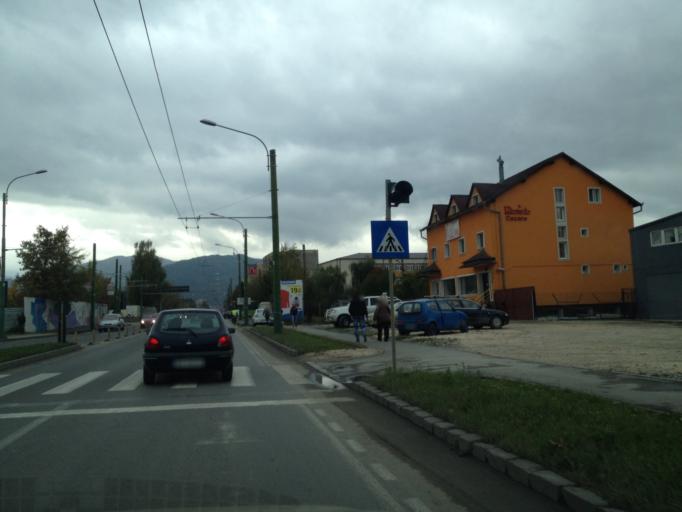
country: RO
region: Brasov
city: Brasov
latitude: 45.6713
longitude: 25.6113
